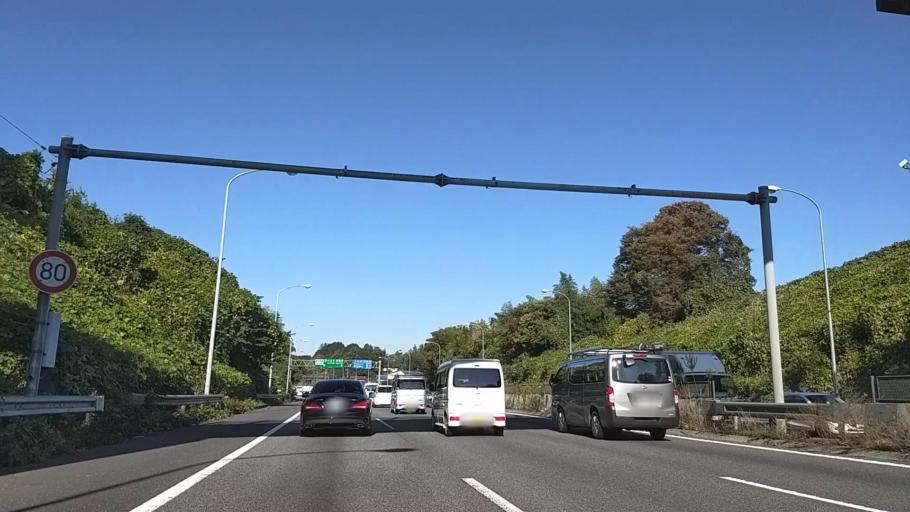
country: JP
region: Kanagawa
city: Minami-rinkan
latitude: 35.4916
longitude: 139.5035
